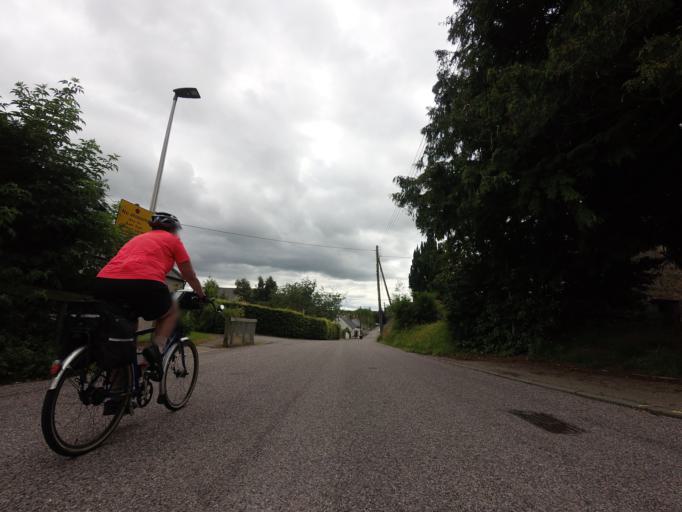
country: GB
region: Scotland
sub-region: Moray
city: Forres
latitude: 57.6051
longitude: -3.6925
